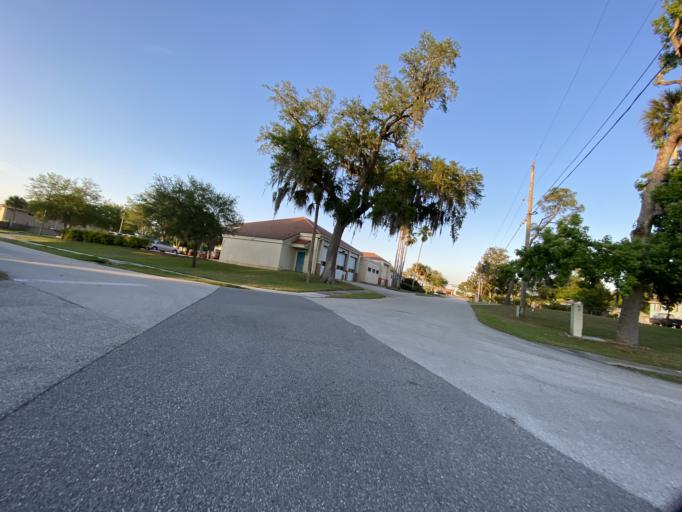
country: US
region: Florida
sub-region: Volusia County
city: South Daytona
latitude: 29.1805
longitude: -81.0085
